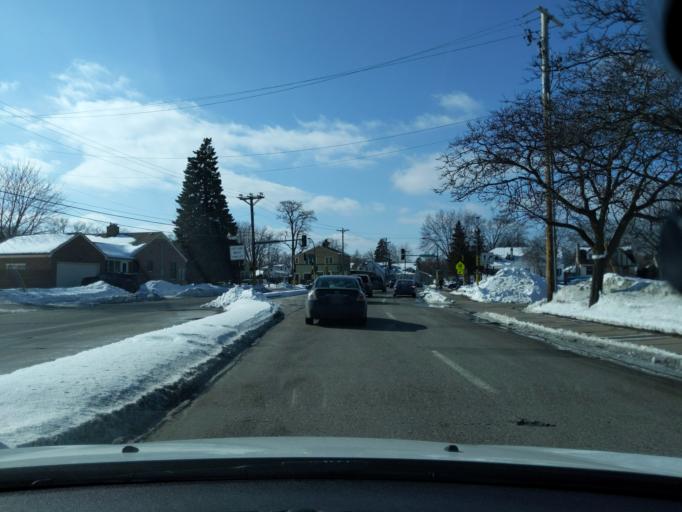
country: US
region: Minnesota
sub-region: Hennepin County
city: Saint Anthony
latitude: 45.0135
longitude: -93.2257
